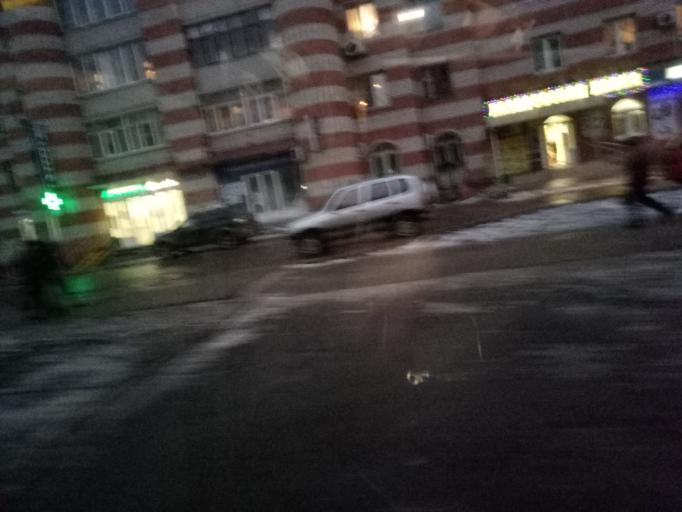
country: RU
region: Tula
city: Tula
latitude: 54.1976
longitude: 37.5847
